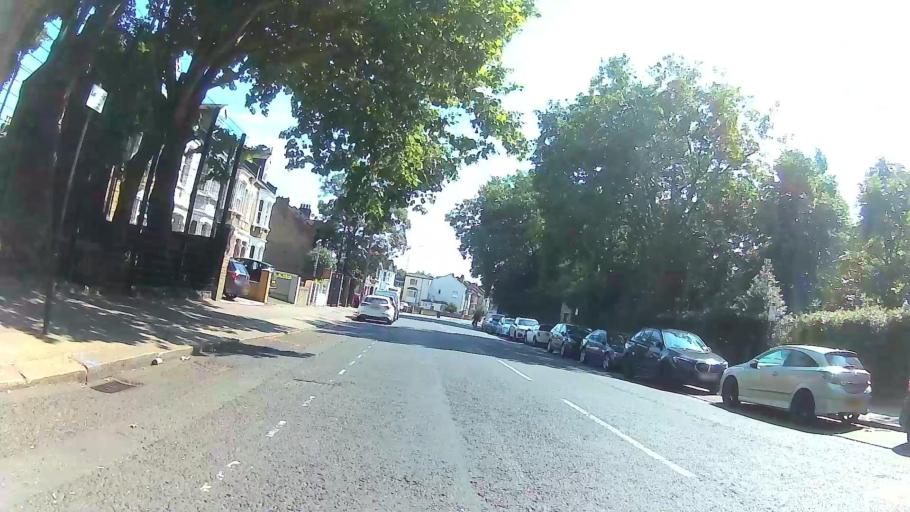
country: GB
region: England
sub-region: Greater London
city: East Ham
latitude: 51.5392
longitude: 0.0229
